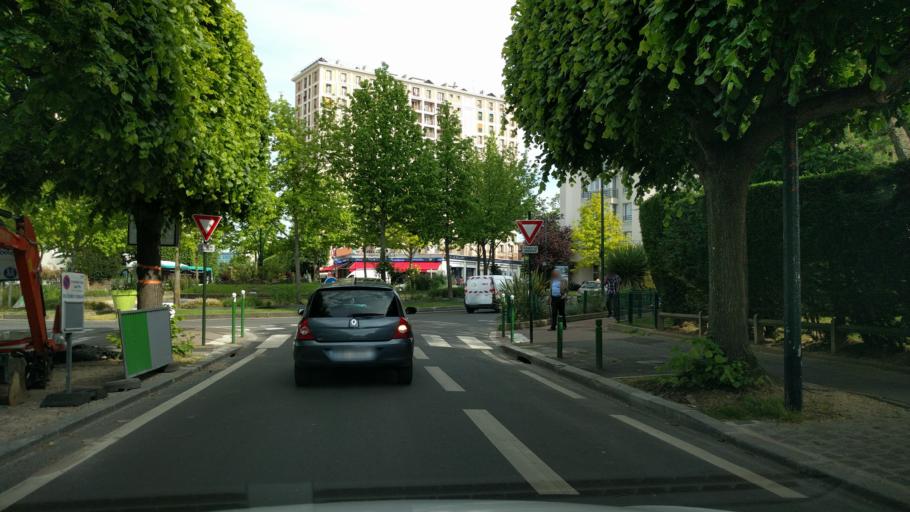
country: FR
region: Ile-de-France
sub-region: Departement des Hauts-de-Seine
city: Chatillon
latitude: 48.8122
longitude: 2.2931
